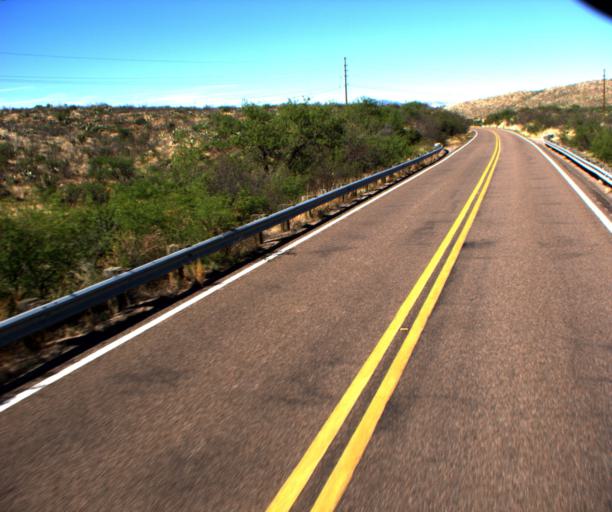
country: US
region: Arizona
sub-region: Pima County
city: Corona de Tucson
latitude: 31.8870
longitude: -110.6710
